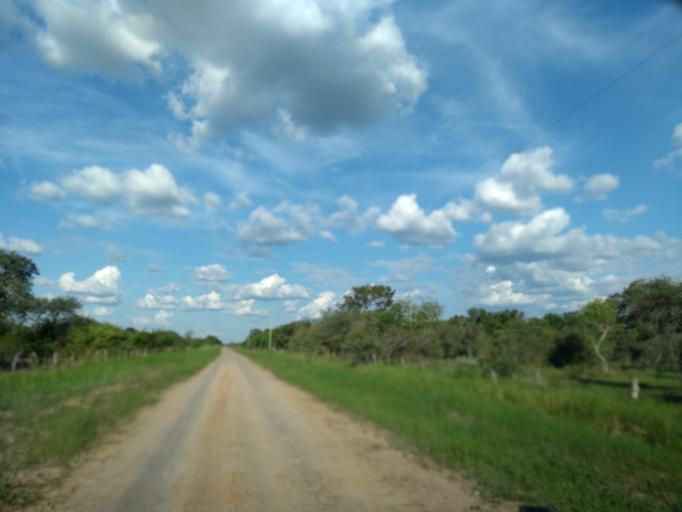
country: AR
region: Chaco
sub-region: Departamento de Quitilipi
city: Quitilipi
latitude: -26.7724
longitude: -60.1995
